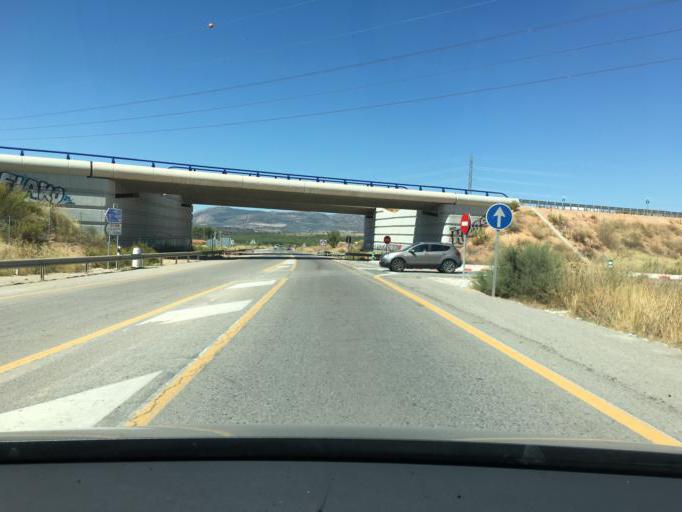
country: ES
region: Andalusia
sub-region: Provincia de Granada
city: Albolote
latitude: 37.2634
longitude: -3.6604
